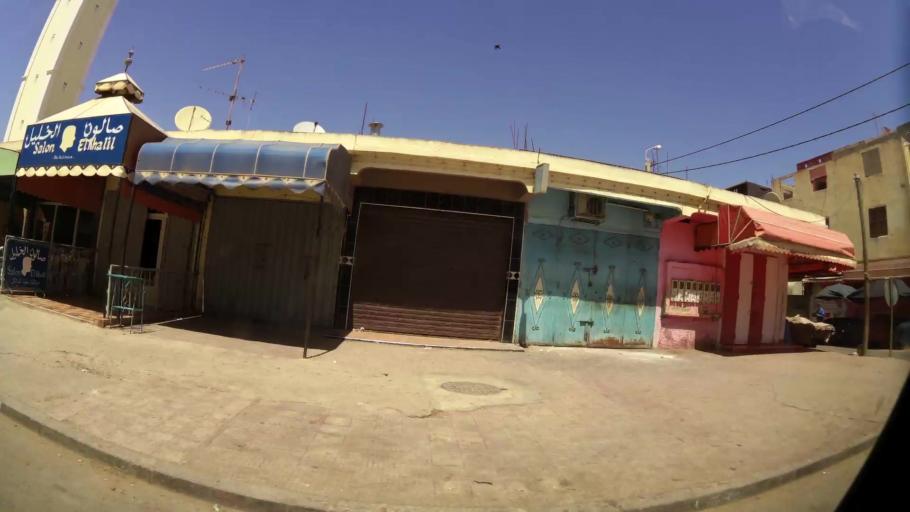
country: MA
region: Souss-Massa-Draa
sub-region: Inezgane-Ait Mellou
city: Inezgane
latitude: 30.3441
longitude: -9.4878
